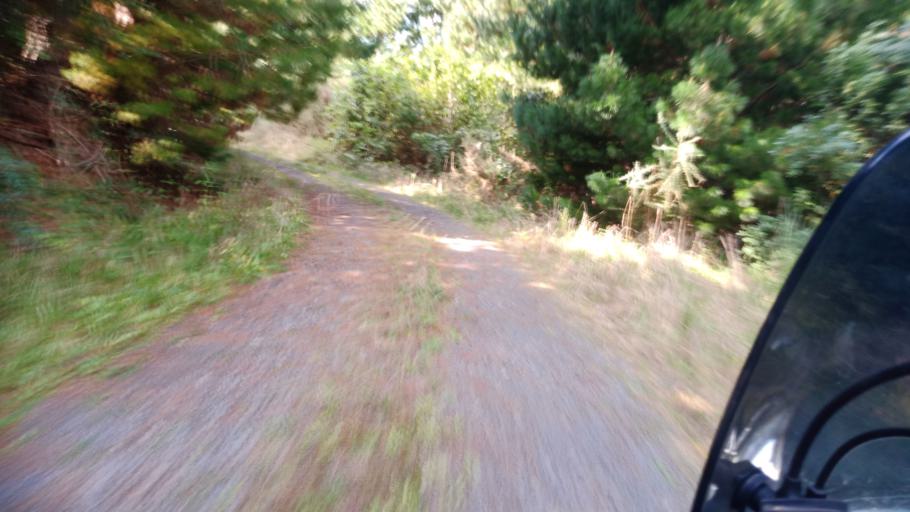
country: NZ
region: Hawke's Bay
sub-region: Wairoa District
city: Wairoa
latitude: -39.0046
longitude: 177.0836
